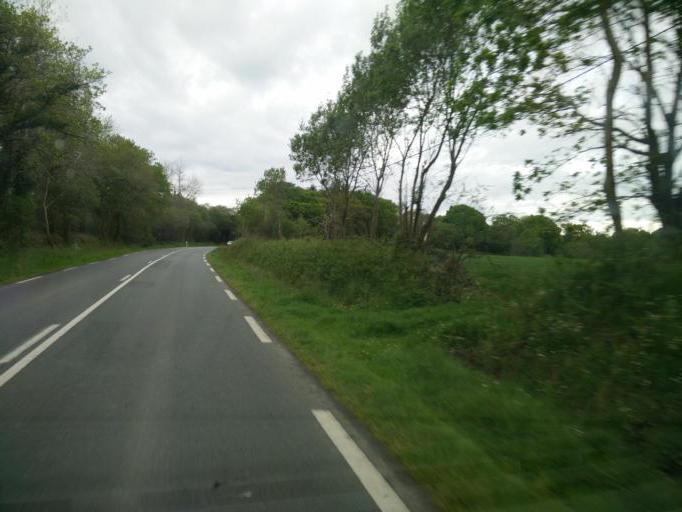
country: FR
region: Brittany
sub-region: Departement des Cotes-d'Armor
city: Ploumilliau
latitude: 48.7043
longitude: -3.5099
